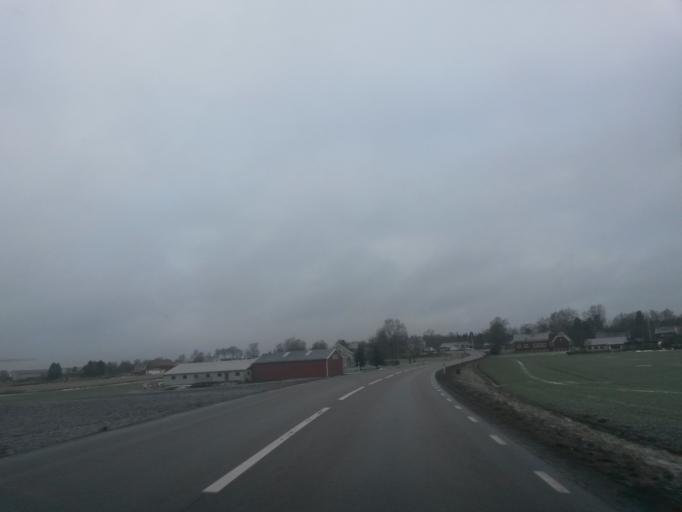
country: SE
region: Vaestra Goetaland
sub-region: Alingsas Kommun
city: Sollebrunn
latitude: 58.1117
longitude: 12.6363
